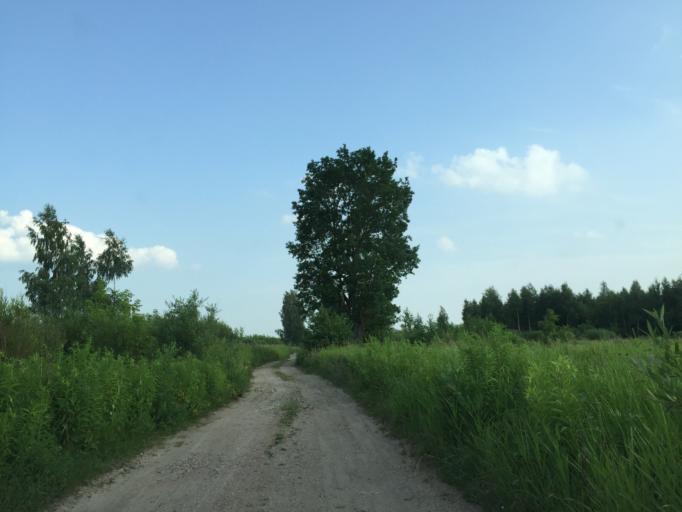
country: LV
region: Jelgava
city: Jelgava
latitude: 56.6712
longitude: 23.7116
